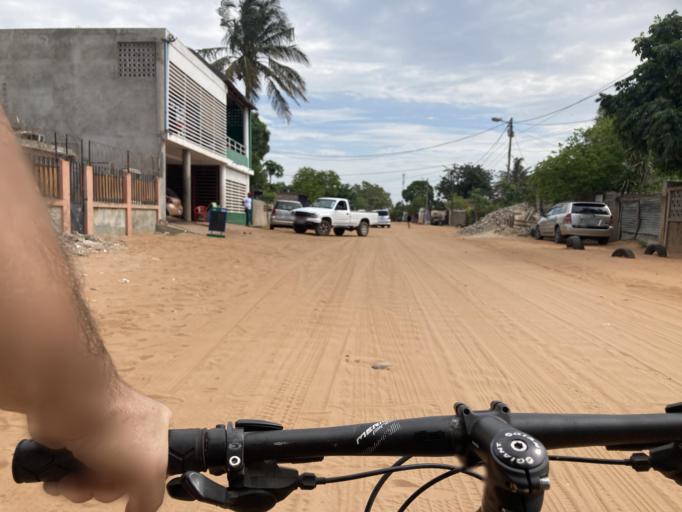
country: MZ
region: Maputo City
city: Maputo
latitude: -25.8975
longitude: 32.6068
